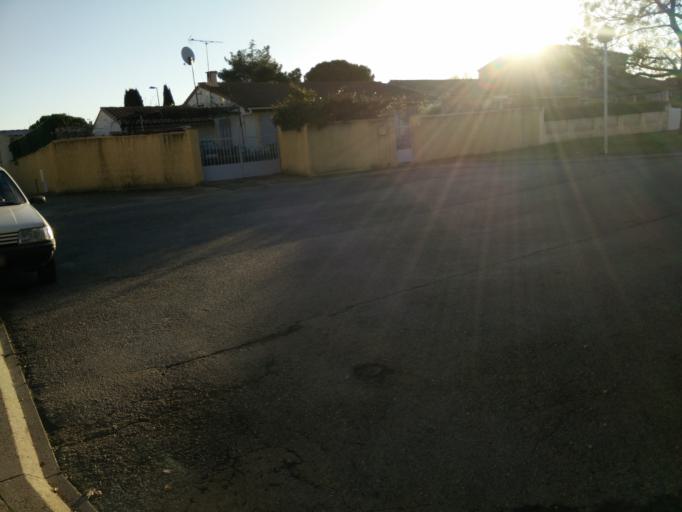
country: FR
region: Languedoc-Roussillon
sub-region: Departement du Gard
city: Aimargues
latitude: 43.6913
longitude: 4.2049
